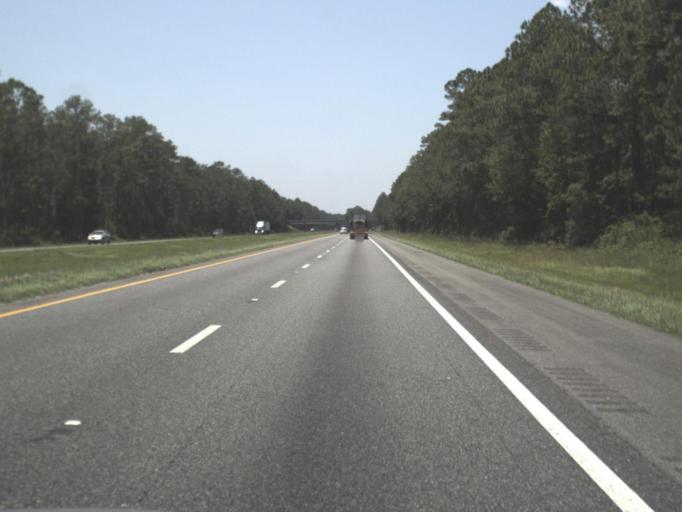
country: US
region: Florida
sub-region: Columbia County
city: Watertown
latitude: 30.2553
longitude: -82.4398
